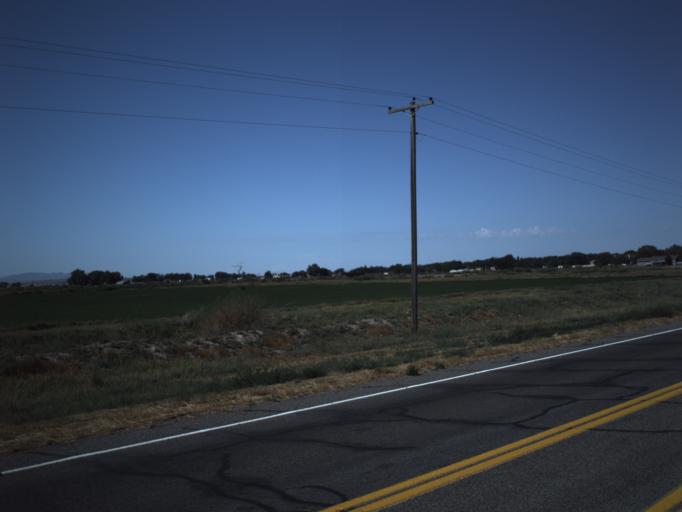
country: US
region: Utah
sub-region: Millard County
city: Delta
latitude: 39.3308
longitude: -112.6549
